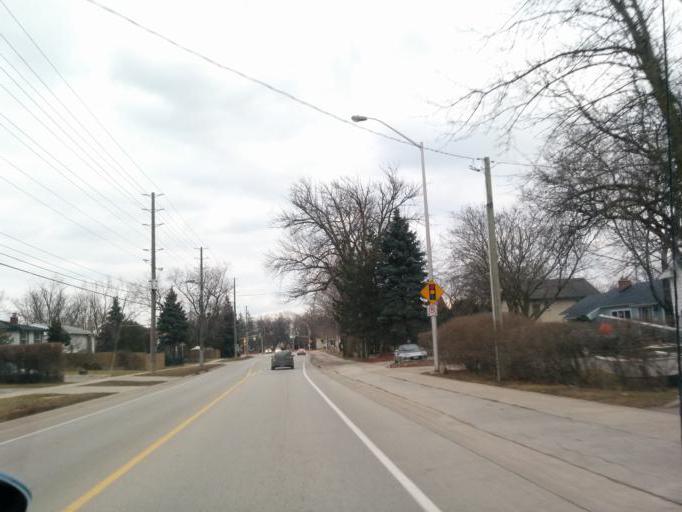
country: CA
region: Ontario
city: Oakville
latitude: 43.3981
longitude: -79.7231
